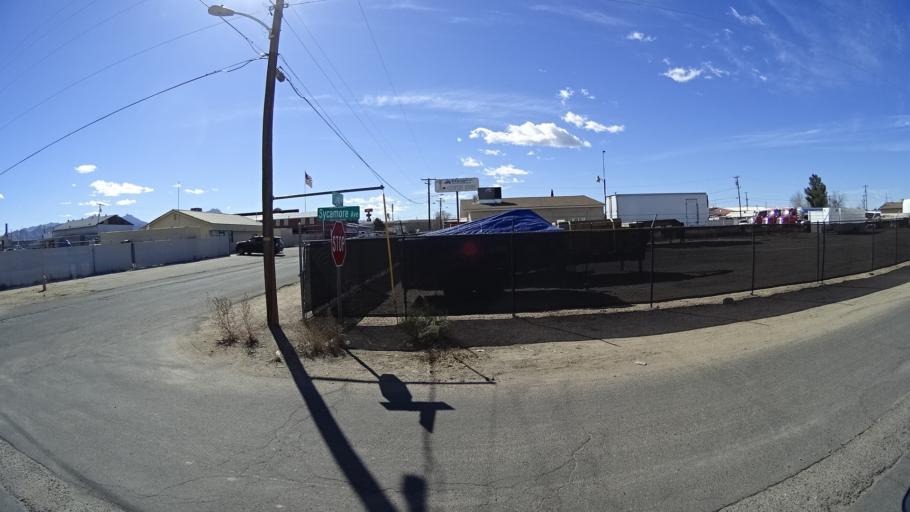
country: US
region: Arizona
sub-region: Mohave County
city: New Kingman-Butler
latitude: 35.2222
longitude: -114.0094
